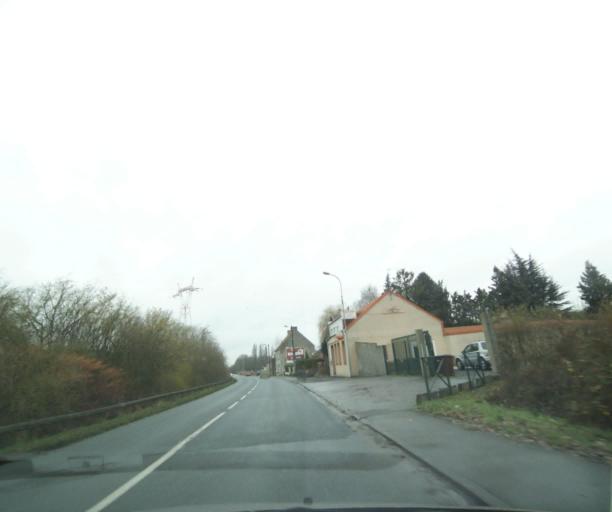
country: FR
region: Nord-Pas-de-Calais
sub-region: Departement du Nord
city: Haulchin
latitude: 50.3283
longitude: 3.4313
